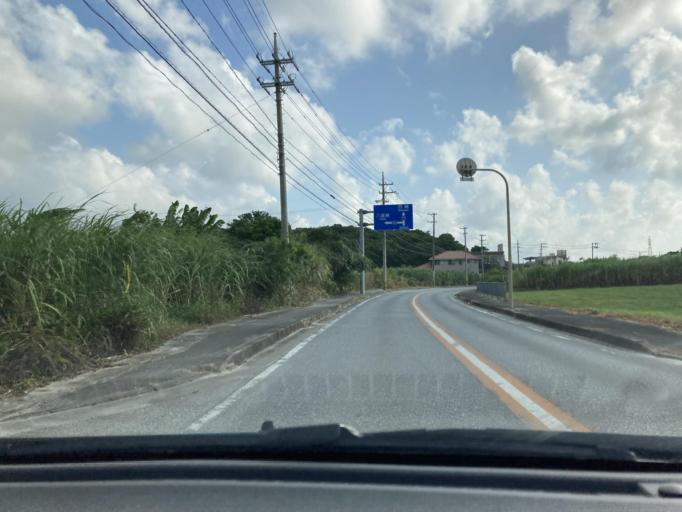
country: JP
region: Okinawa
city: Itoman
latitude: 26.1394
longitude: 127.7007
